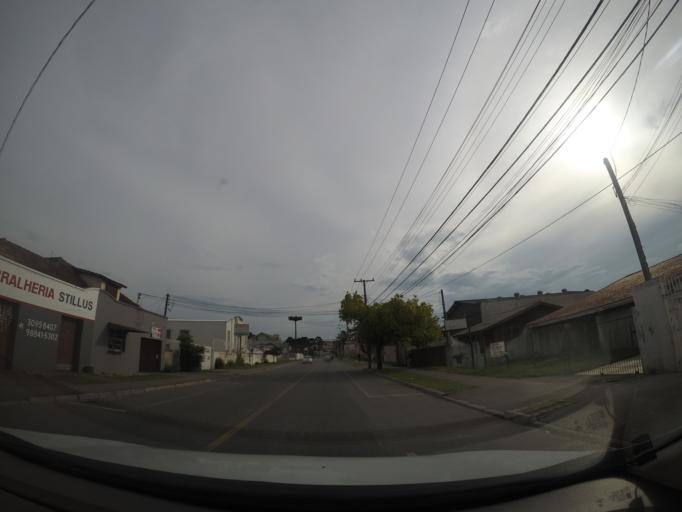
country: BR
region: Parana
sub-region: Sao Jose Dos Pinhais
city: Sao Jose dos Pinhais
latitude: -25.5055
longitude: -49.2320
